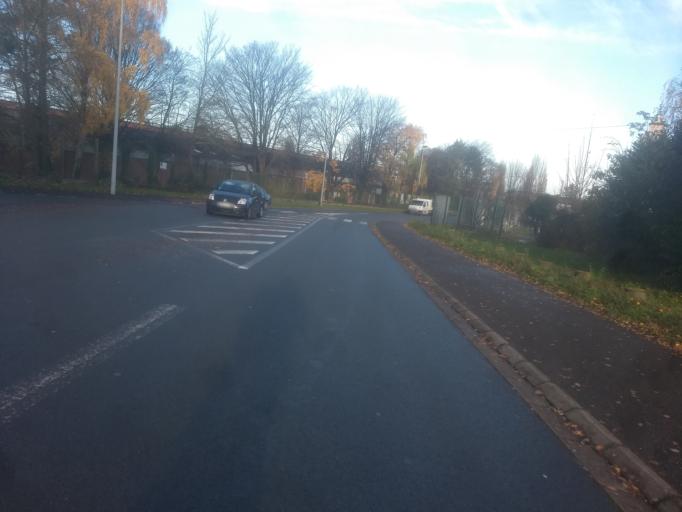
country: FR
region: Nord-Pas-de-Calais
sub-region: Departement du Pas-de-Calais
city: Anzin-Saint-Aubin
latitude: 50.2972
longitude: 2.7385
